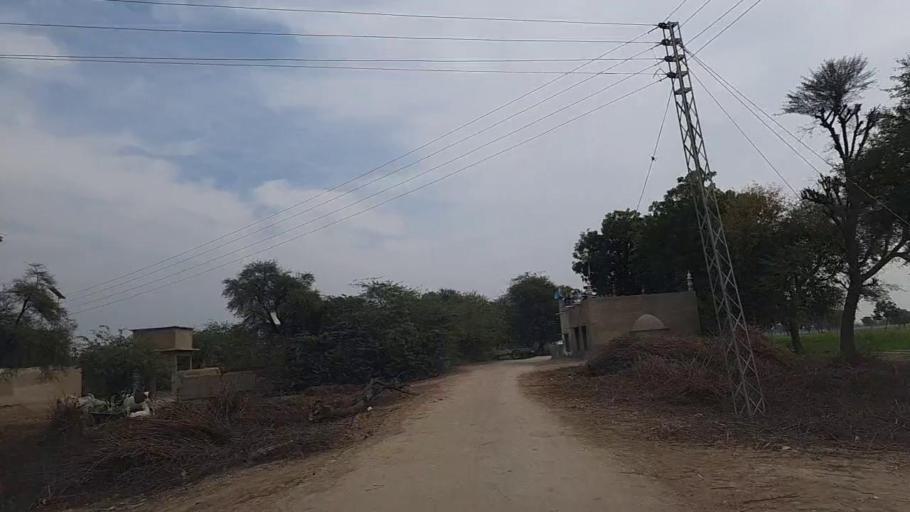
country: PK
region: Sindh
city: Daur
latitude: 26.4453
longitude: 68.4573
